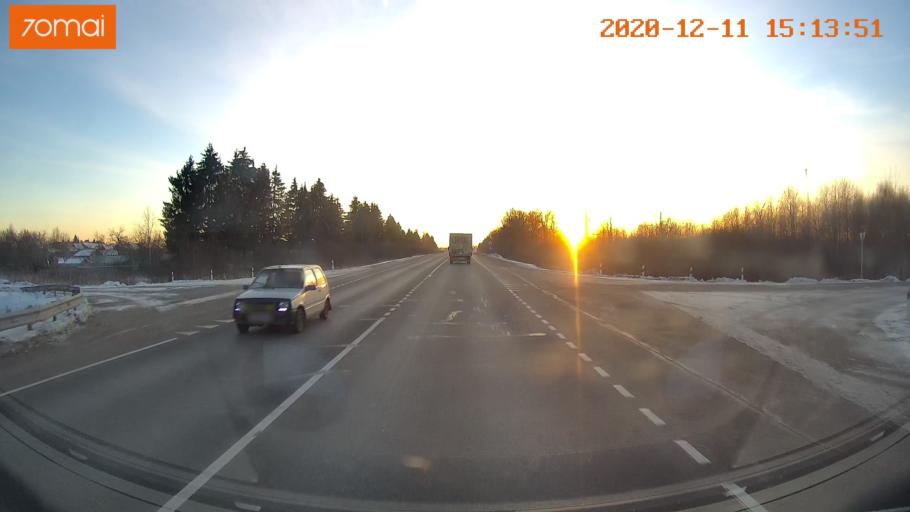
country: RU
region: Ivanovo
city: Furmanov
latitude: 57.2409
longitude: 41.1461
